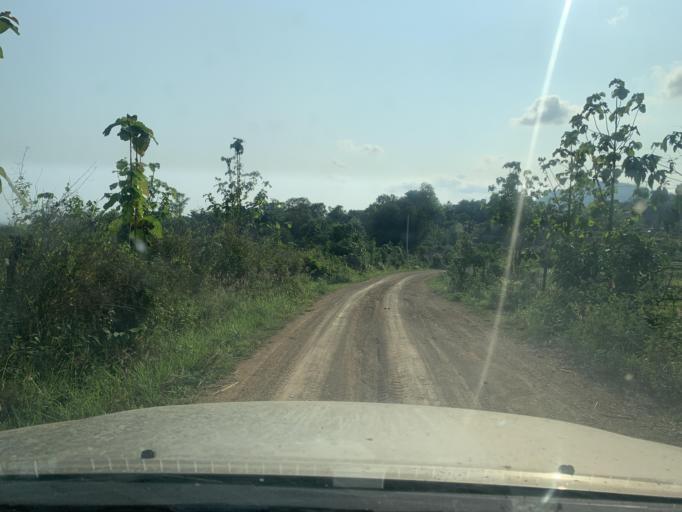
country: TH
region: Uttaradit
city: Ban Khok
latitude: 18.2780
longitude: 101.3098
